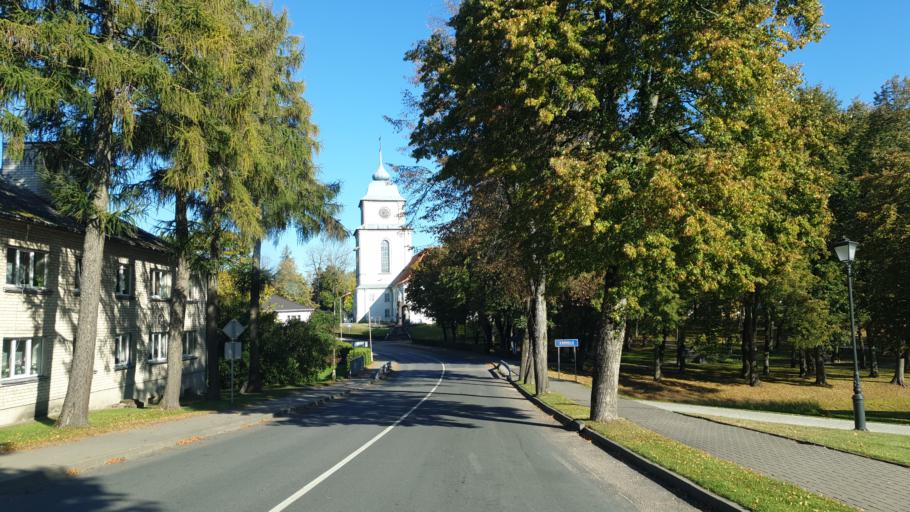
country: LT
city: Varniai
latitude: 55.7425
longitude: 22.3718
